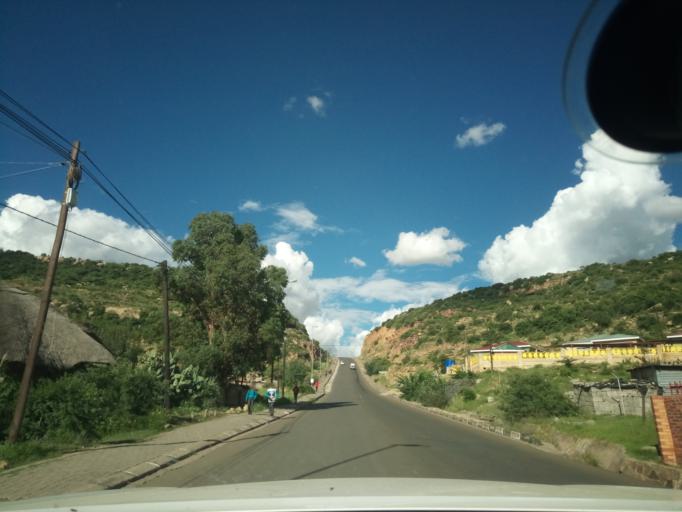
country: LS
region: Maseru
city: Maseru
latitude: -29.3313
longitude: 27.4895
